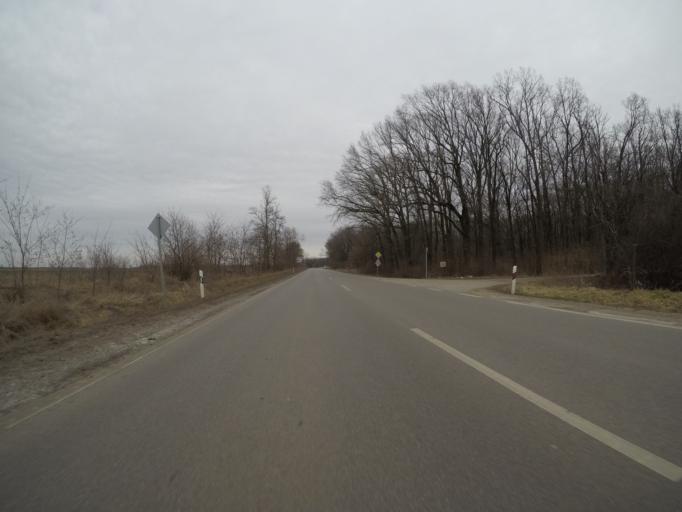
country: HU
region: Jasz-Nagykun-Szolnok
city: Jaszjakohalma
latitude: 47.5138
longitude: 20.0489
